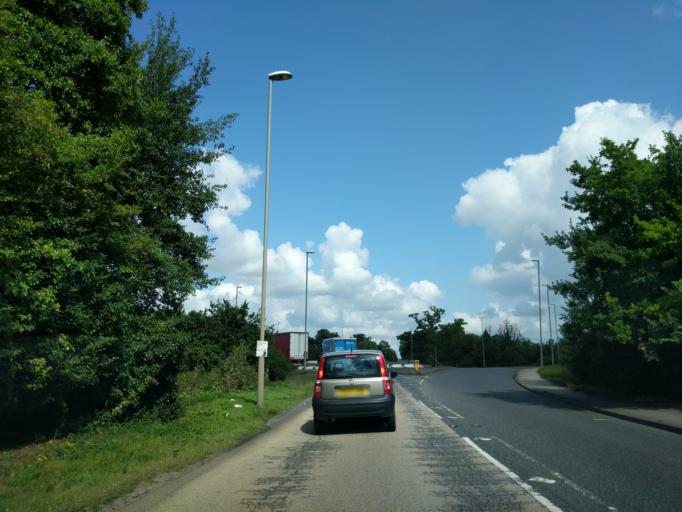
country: GB
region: England
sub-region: Suffolk
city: Exning
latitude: 52.2941
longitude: 0.3898
